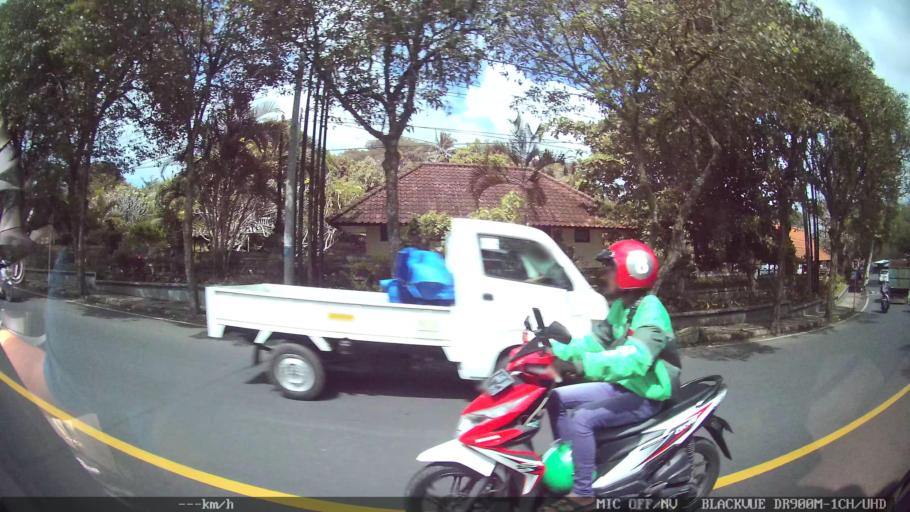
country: ID
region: Bali
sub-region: Kabupaten Gianyar
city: Ubud
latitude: -8.5231
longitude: 115.2874
